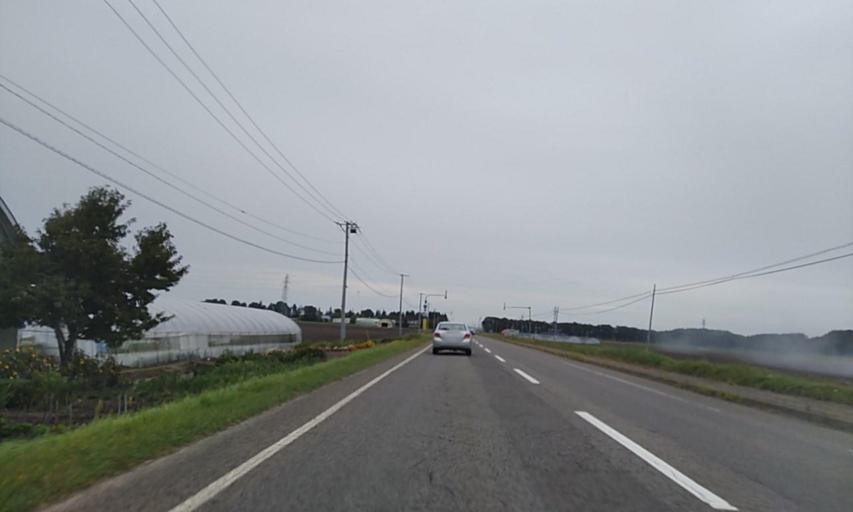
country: JP
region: Hokkaido
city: Bihoro
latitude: 43.8553
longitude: 144.1223
